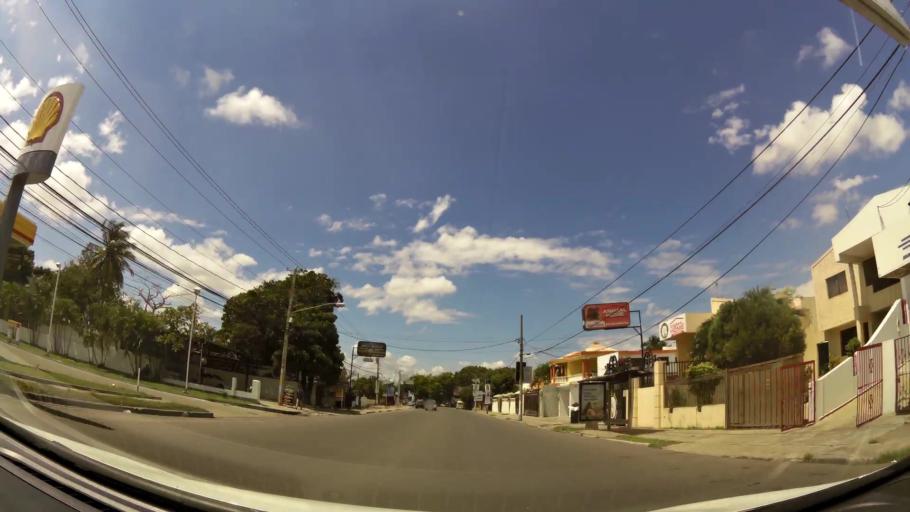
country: DO
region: Santiago
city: Santiago de los Caballeros
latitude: 19.4663
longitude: -70.6647
